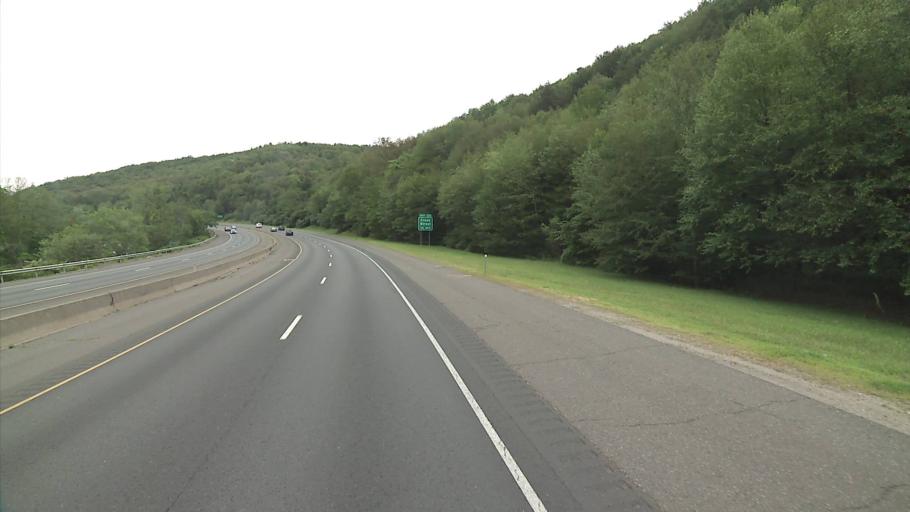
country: US
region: Connecticut
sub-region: New Haven County
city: Naugatuck
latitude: 41.4593
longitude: -73.0558
